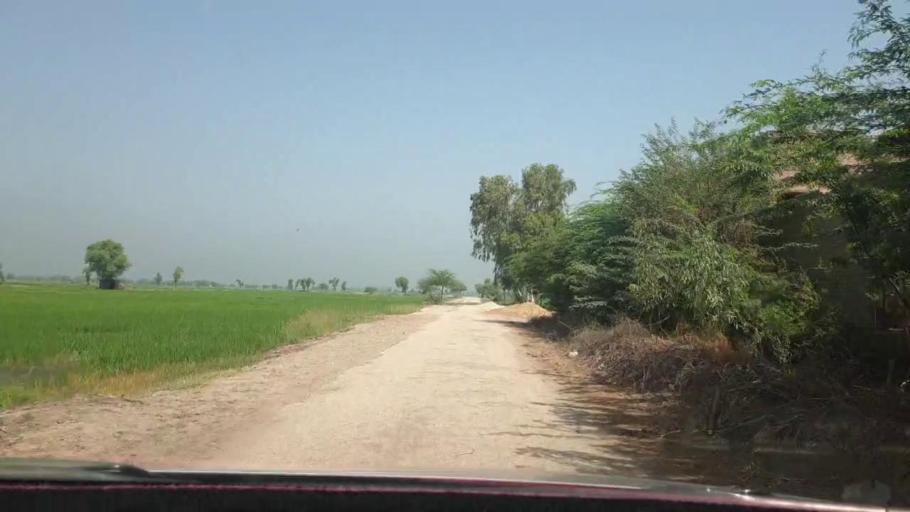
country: PK
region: Sindh
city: Nasirabad
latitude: 27.4263
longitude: 67.9046
